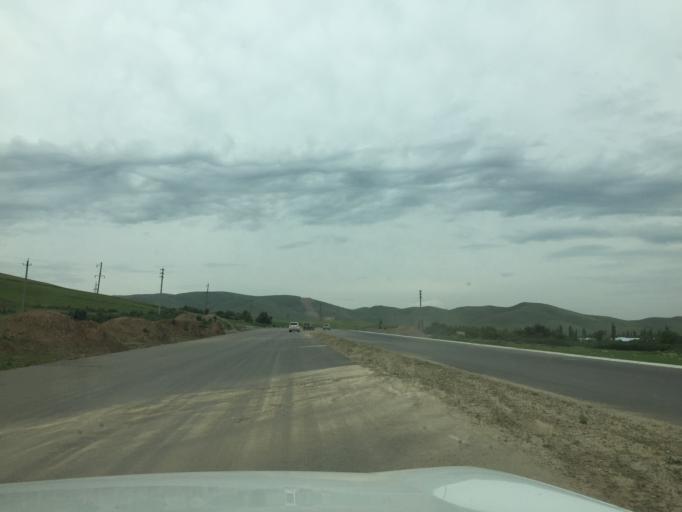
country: KZ
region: Ongtustik Qazaqstan
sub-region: Tulkibas Audany
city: Zhabagly
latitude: 42.5131
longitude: 70.5289
